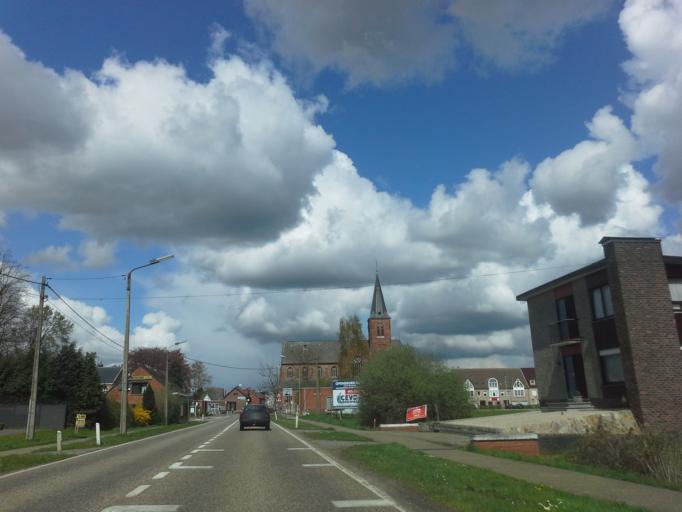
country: BE
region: Flanders
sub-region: Provincie Limburg
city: Tessenderlo
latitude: 51.0842
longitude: 5.0707
